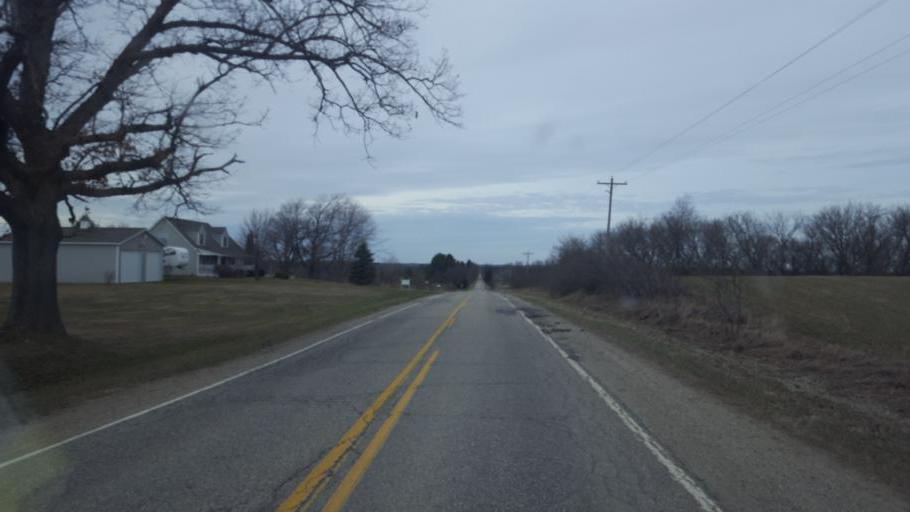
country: US
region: Michigan
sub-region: Montcalm County
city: Edmore
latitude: 43.4665
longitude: -85.0051
